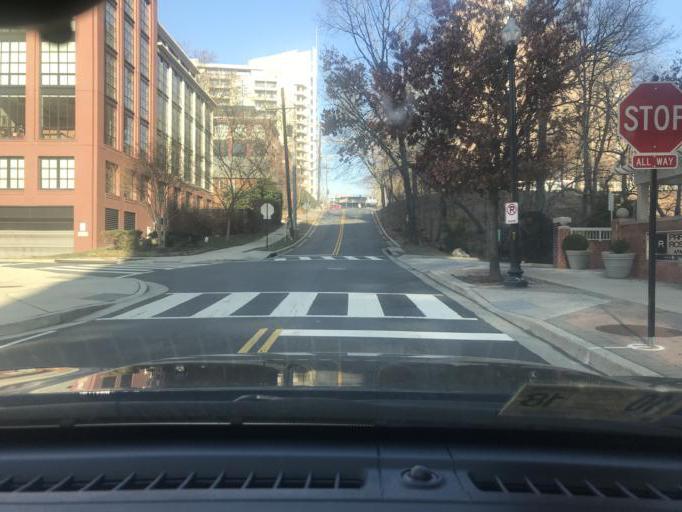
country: US
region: Virginia
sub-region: Arlington County
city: Arlington
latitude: 38.8926
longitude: -77.0769
